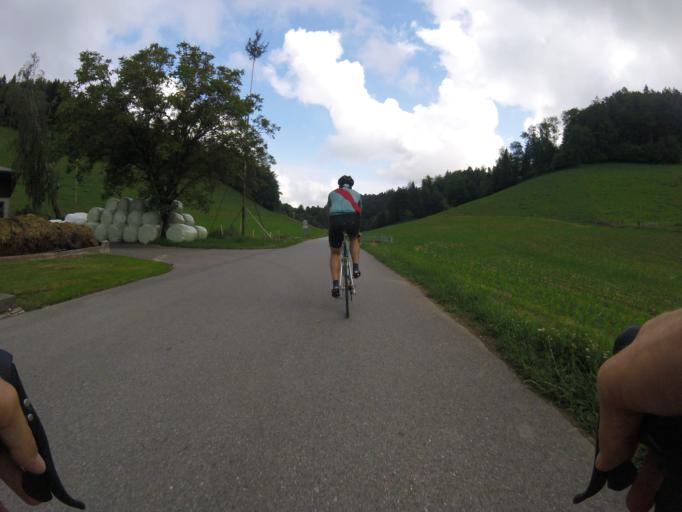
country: CH
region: Bern
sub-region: Emmental District
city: Krauchthal
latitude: 46.9808
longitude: 7.5817
